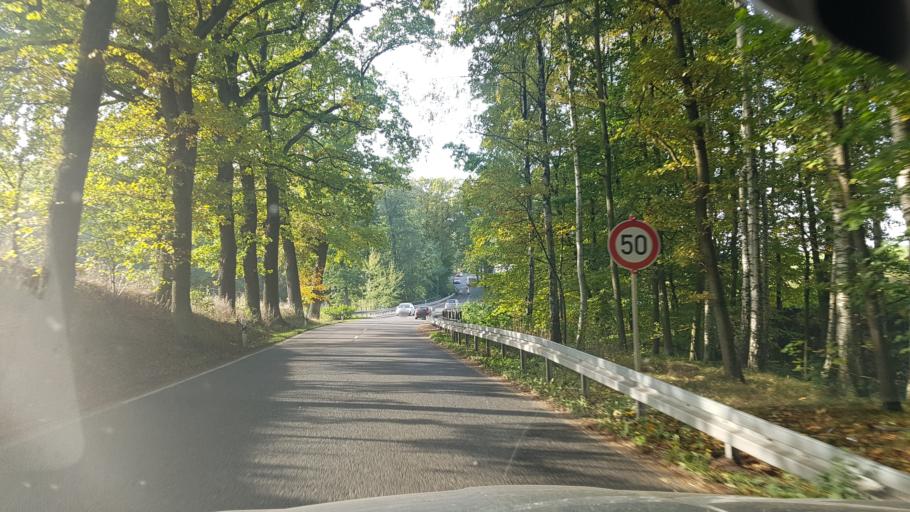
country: DE
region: Saxony
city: Struppen
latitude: 50.9271
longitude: 14.0362
